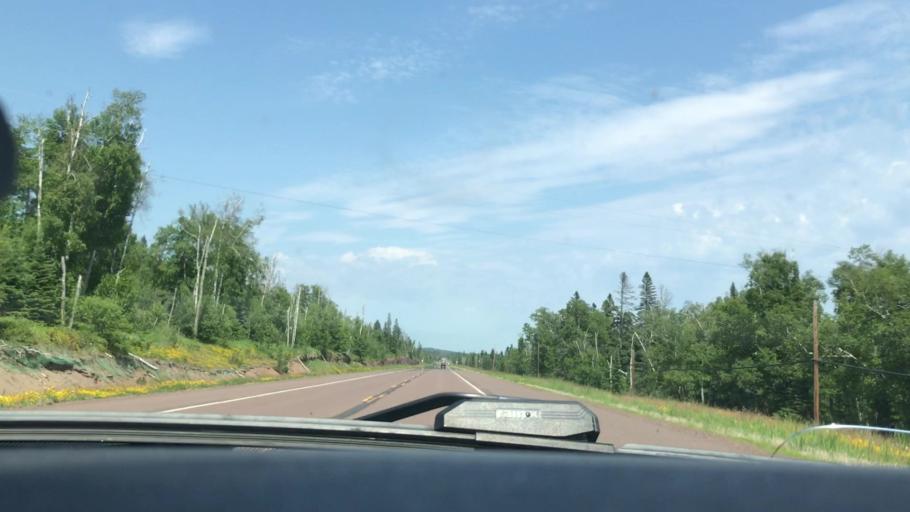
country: US
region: Minnesota
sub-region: Cook County
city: Grand Marais
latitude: 47.6222
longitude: -90.7452
